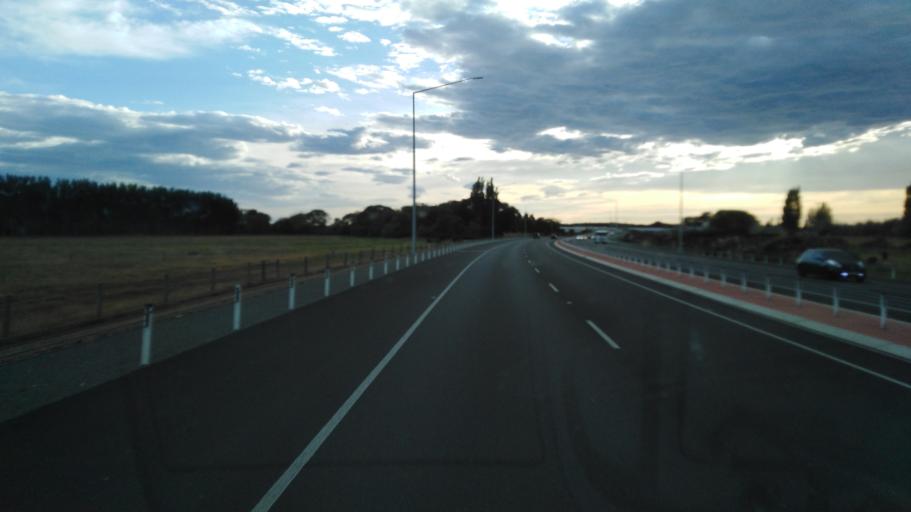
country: NZ
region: Canterbury
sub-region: Waimakariri District
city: Kaiapoi
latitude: -43.4383
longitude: 172.6251
